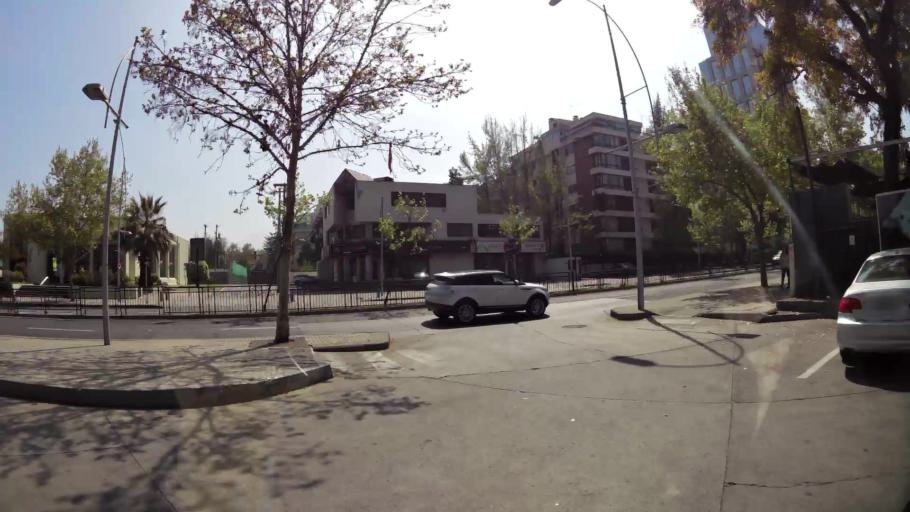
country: CL
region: Santiago Metropolitan
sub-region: Provincia de Santiago
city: Villa Presidente Frei, Nunoa, Santiago, Chile
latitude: -33.3995
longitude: -70.5894
